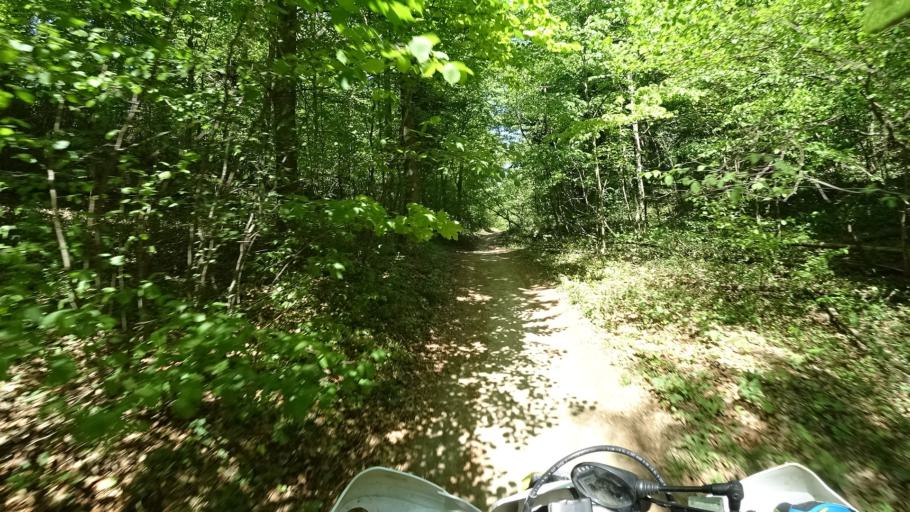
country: HR
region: Zagrebacka
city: Jablanovec
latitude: 45.8676
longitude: 15.8542
